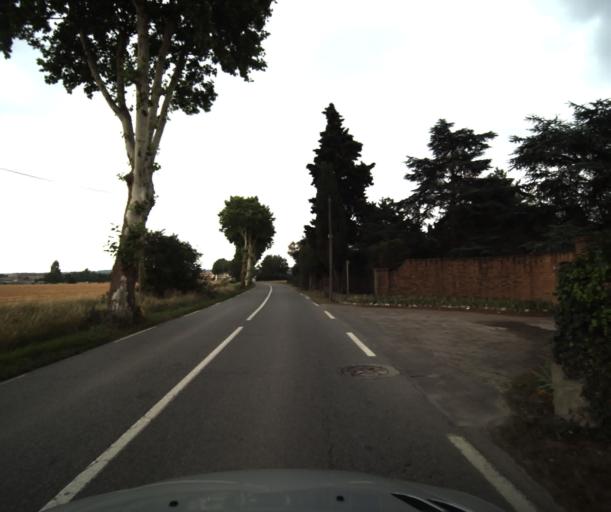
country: FR
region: Midi-Pyrenees
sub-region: Departement de la Haute-Garonne
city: Pinsaguel
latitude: 43.5240
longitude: 1.3914
